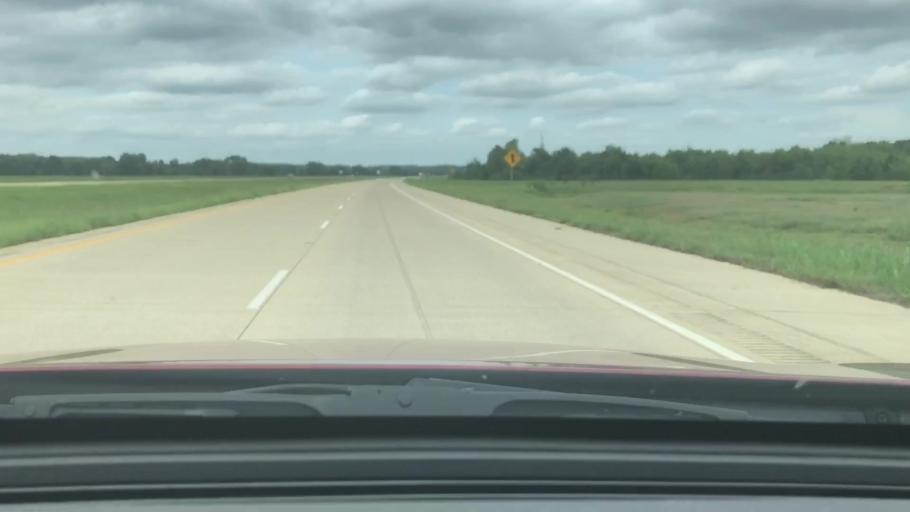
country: US
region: Louisiana
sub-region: Caddo Parish
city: Oil City
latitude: 32.7687
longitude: -93.8888
